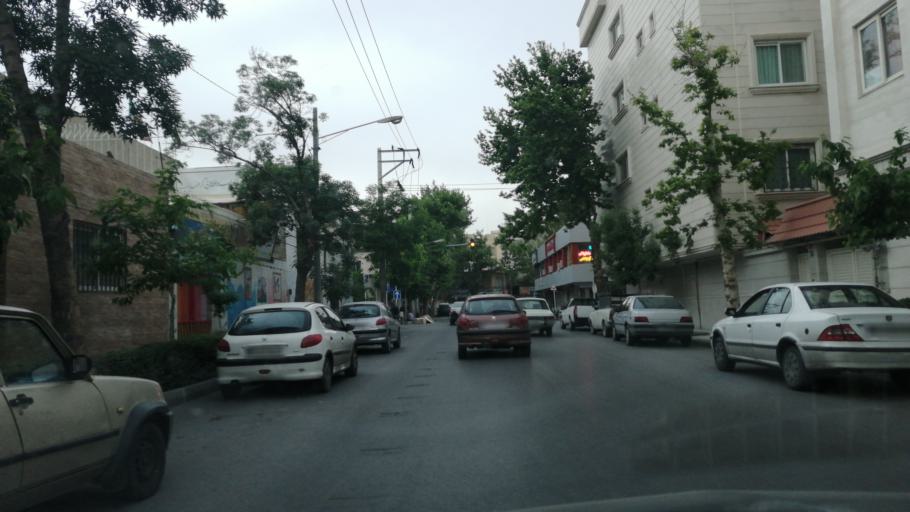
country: IR
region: Razavi Khorasan
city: Mashhad
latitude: 36.2961
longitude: 59.5820
